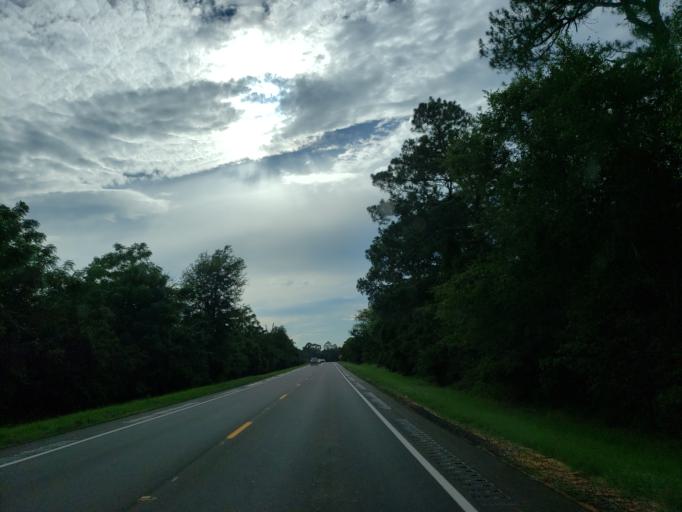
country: US
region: Georgia
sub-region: Irwin County
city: Ocilla
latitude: 31.5641
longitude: -83.3345
